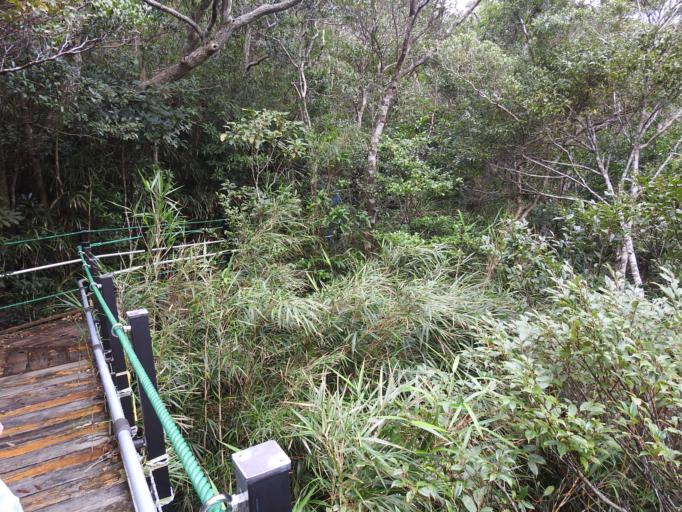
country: JP
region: Okinawa
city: Nago
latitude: 26.7219
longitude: 128.2659
